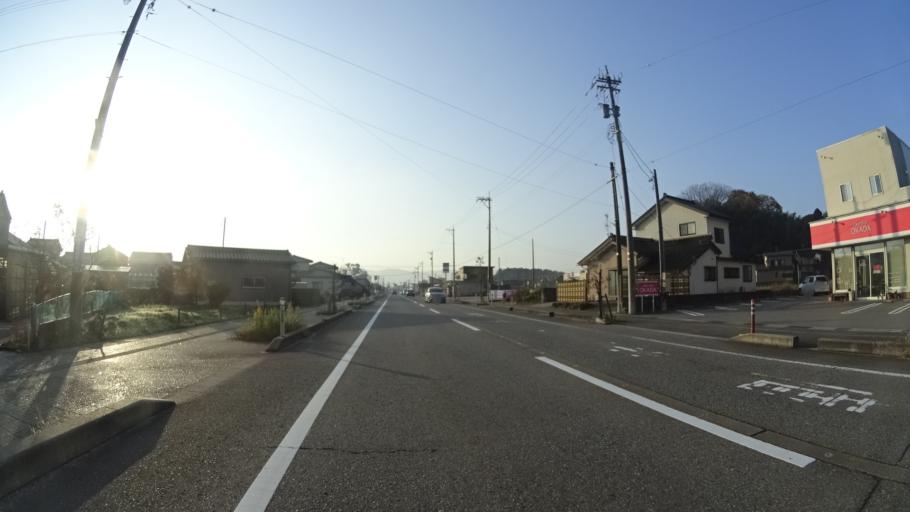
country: JP
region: Ishikawa
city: Nanao
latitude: 37.0506
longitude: 136.9565
